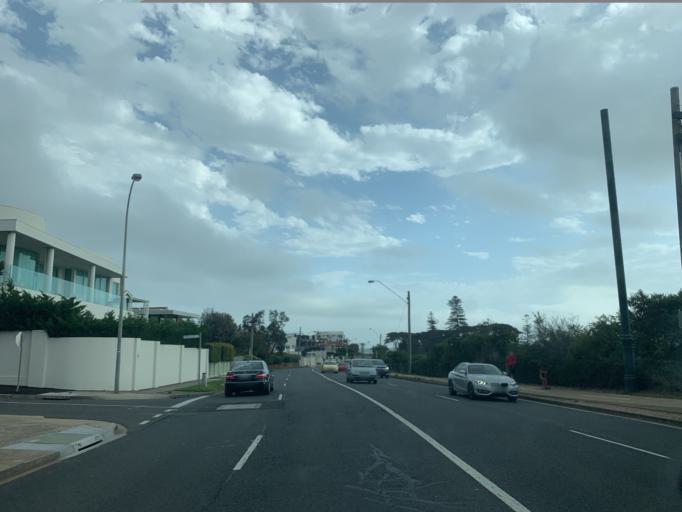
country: AU
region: Victoria
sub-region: Bayside
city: Hampton
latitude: -37.9224
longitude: 144.9879
